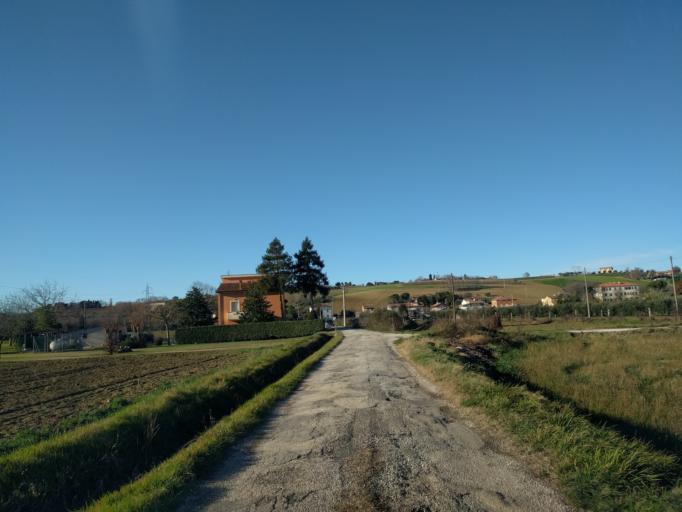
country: IT
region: The Marches
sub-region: Provincia di Pesaro e Urbino
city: Cuccurano
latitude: 43.7859
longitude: 12.9492
